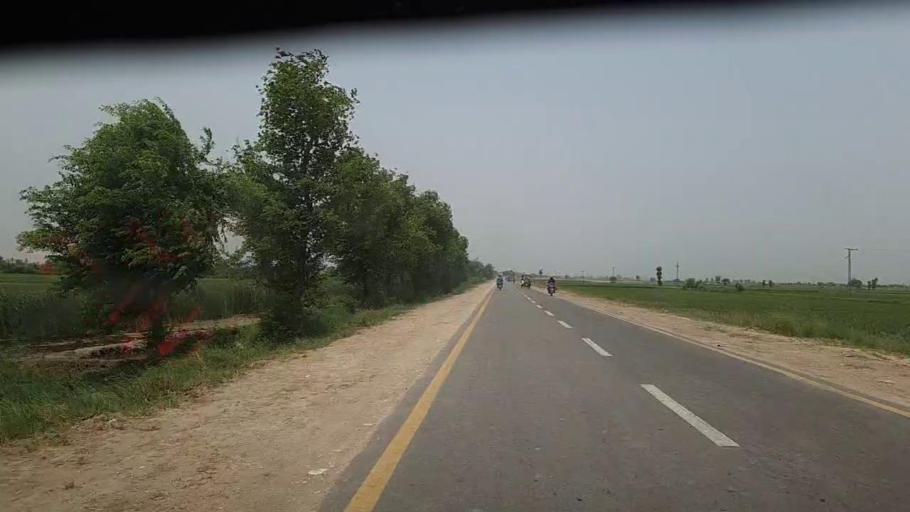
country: PK
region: Sindh
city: Sita Road
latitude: 27.0409
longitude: 67.8657
